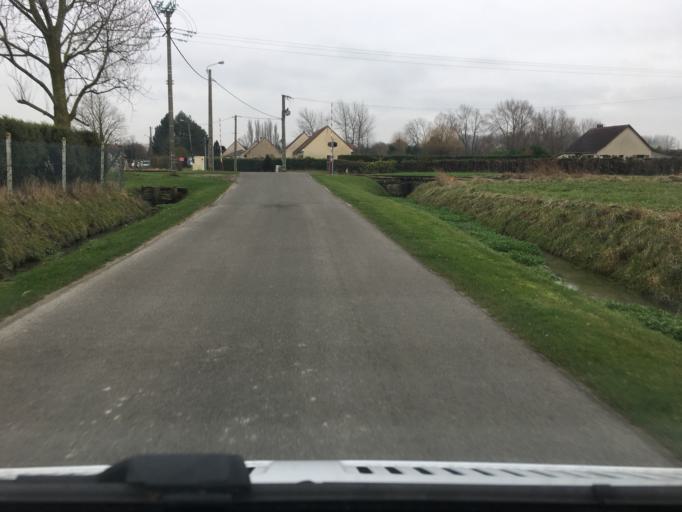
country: FR
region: Picardie
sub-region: Departement de la Somme
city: Pende
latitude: 50.1671
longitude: 1.5523
